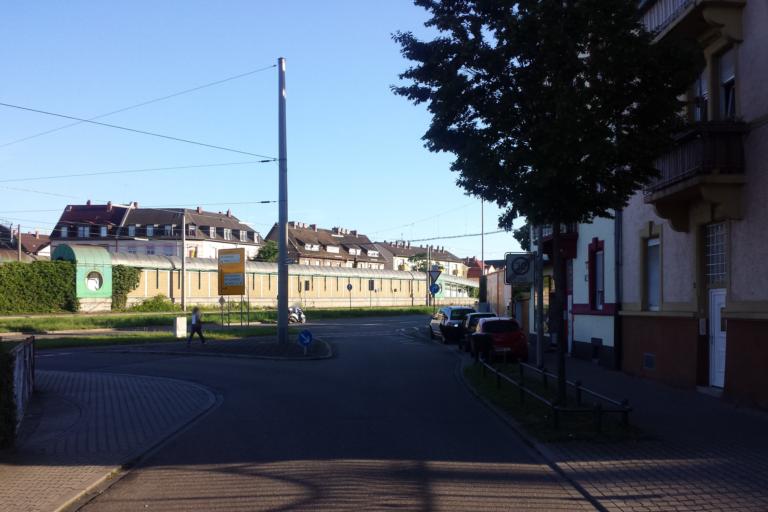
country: DE
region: Baden-Wuerttemberg
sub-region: Karlsruhe Region
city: Mannheim
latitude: 49.5178
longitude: 8.4773
